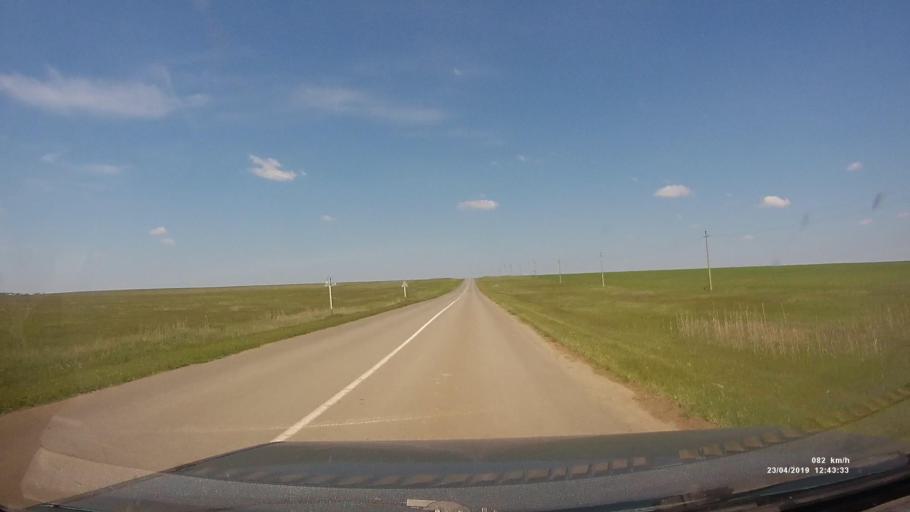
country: RU
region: Kalmykiya
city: Yashalta
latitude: 46.4654
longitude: 42.6502
